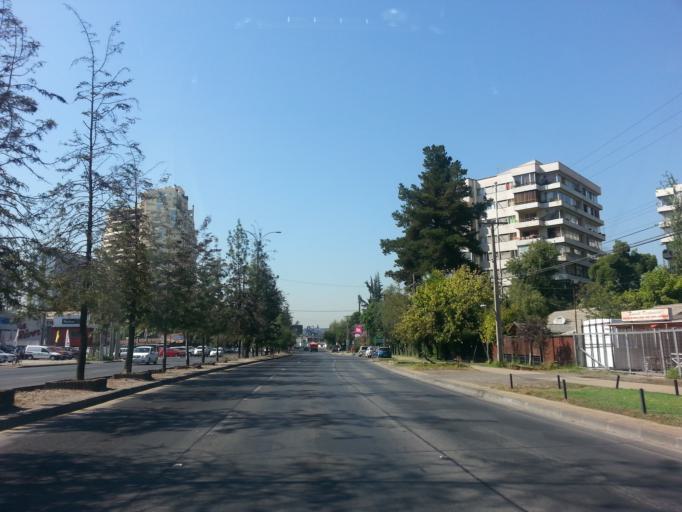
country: CL
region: Santiago Metropolitan
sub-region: Provincia de Santiago
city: Villa Presidente Frei, Nunoa, Santiago, Chile
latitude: -33.4348
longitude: -70.5743
